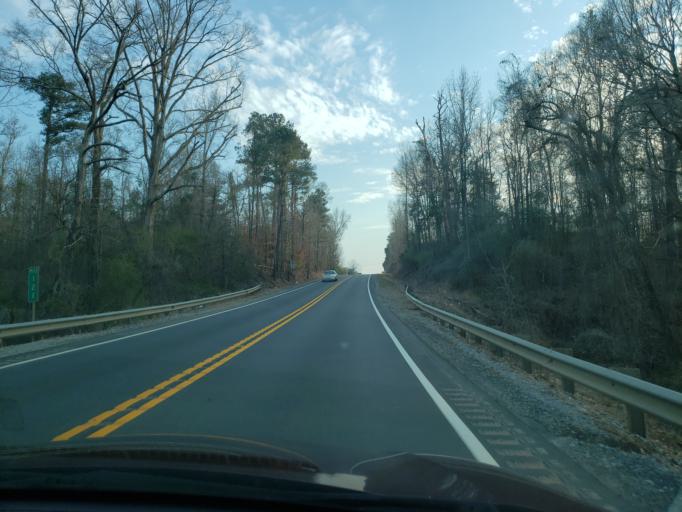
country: US
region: Alabama
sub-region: Hale County
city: Moundville
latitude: 32.8817
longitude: -87.6085
